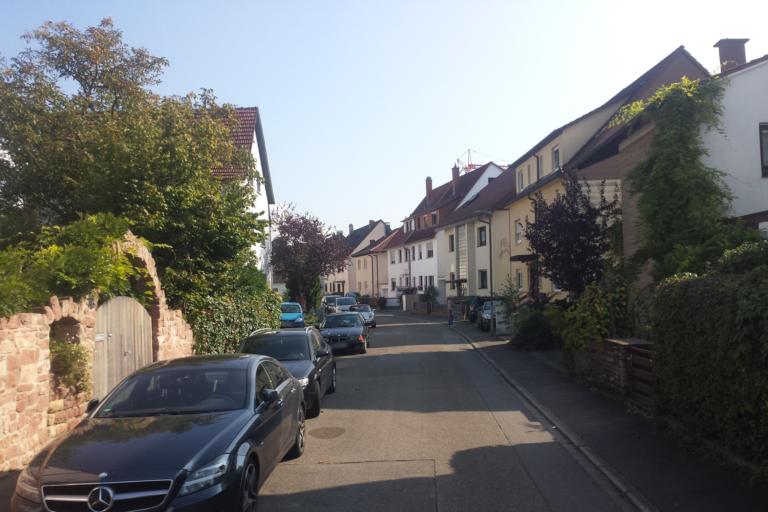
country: DE
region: Baden-Wuerttemberg
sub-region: Karlsruhe Region
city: Ilvesheim
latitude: 49.4778
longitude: 8.5633
